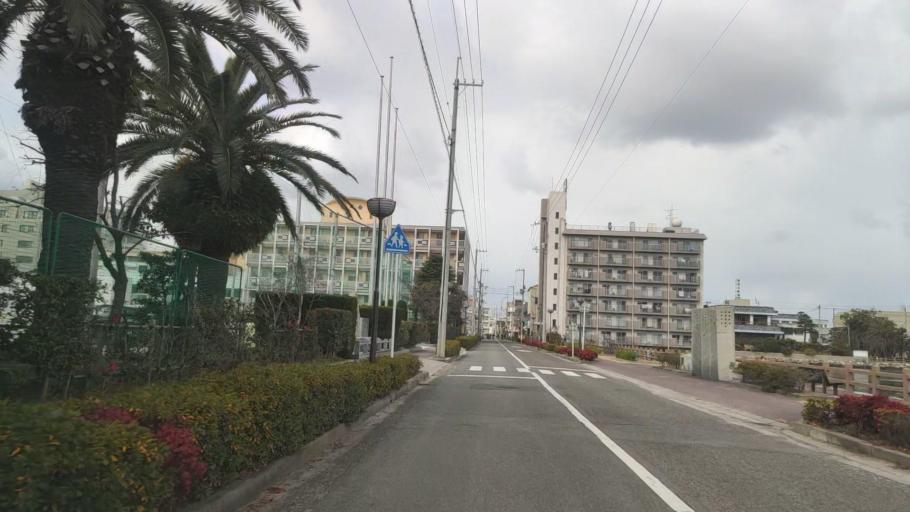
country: JP
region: Ehime
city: Saijo
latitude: 34.0622
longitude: 133.0058
